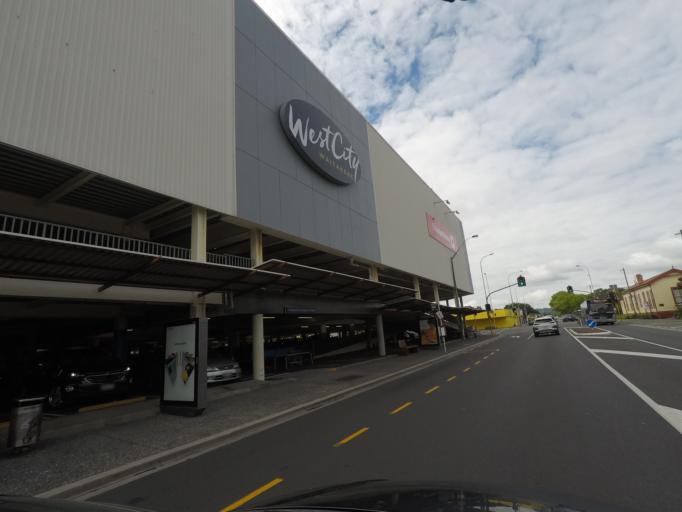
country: NZ
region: Auckland
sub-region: Auckland
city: Rosebank
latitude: -36.8812
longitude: 174.6312
